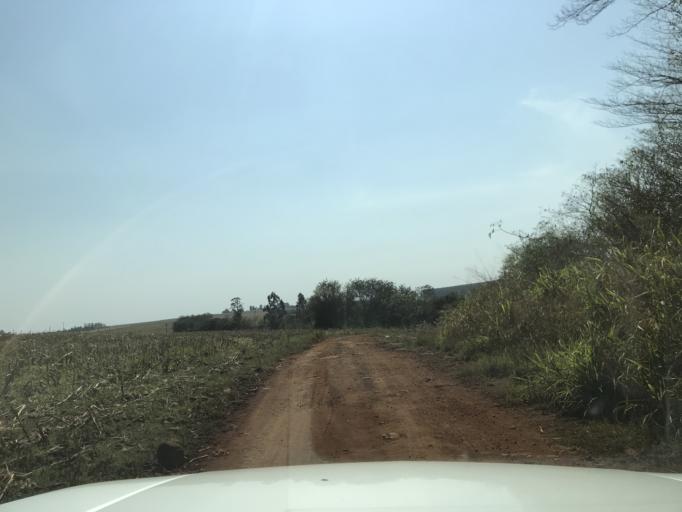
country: BR
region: Parana
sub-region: Palotina
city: Palotina
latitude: -24.2180
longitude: -53.7324
